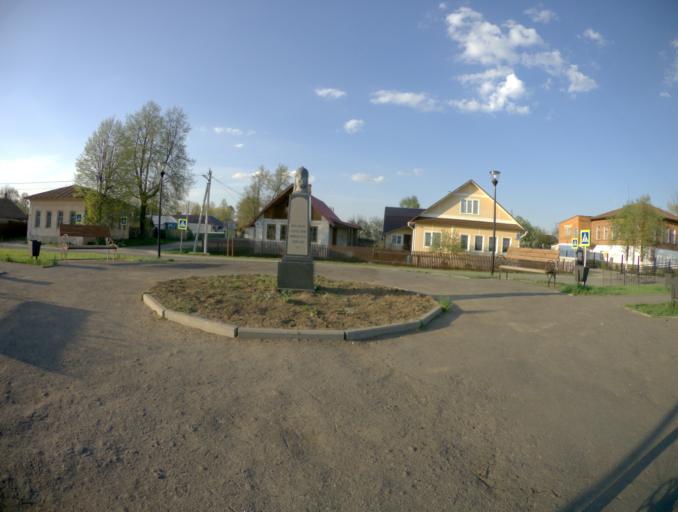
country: RU
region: Ivanovo
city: Yuzha
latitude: 56.5781
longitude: 41.8746
